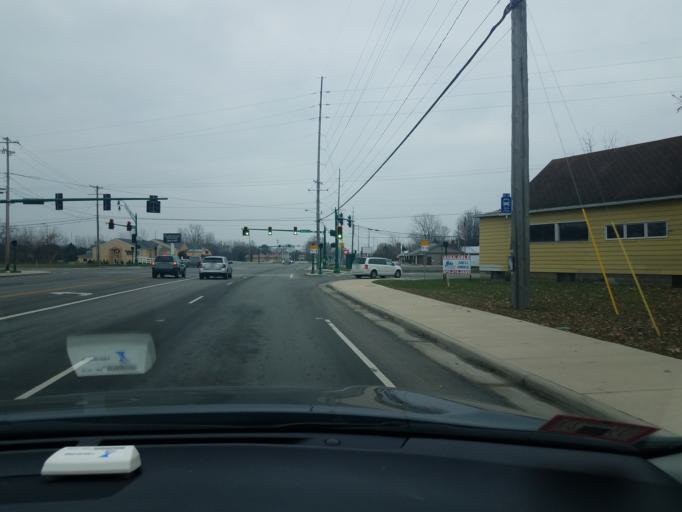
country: US
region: Ohio
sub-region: Erie County
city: Sandusky
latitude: 41.3963
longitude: -82.6521
